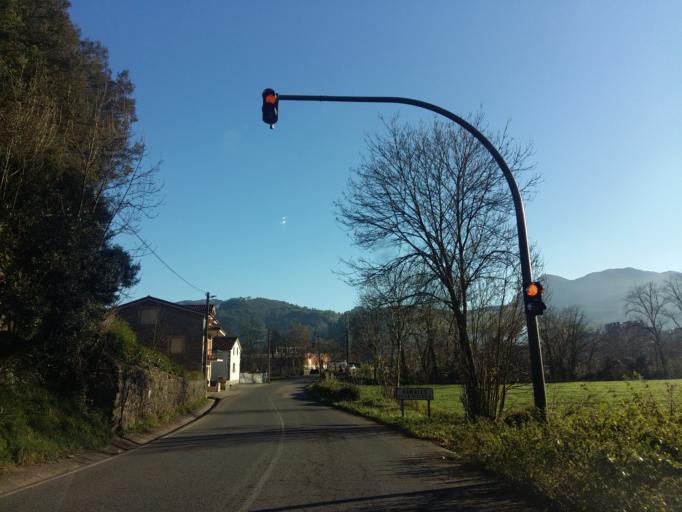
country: ES
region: Cantabria
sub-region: Provincia de Cantabria
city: Ramales de la Victoria
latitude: 43.2613
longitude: -3.4717
